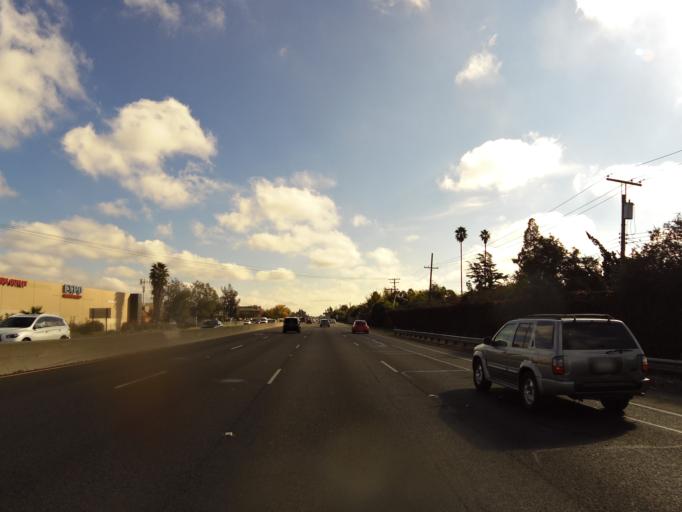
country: US
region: California
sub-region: Sacramento County
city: Parkway
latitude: 38.4921
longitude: -121.4419
